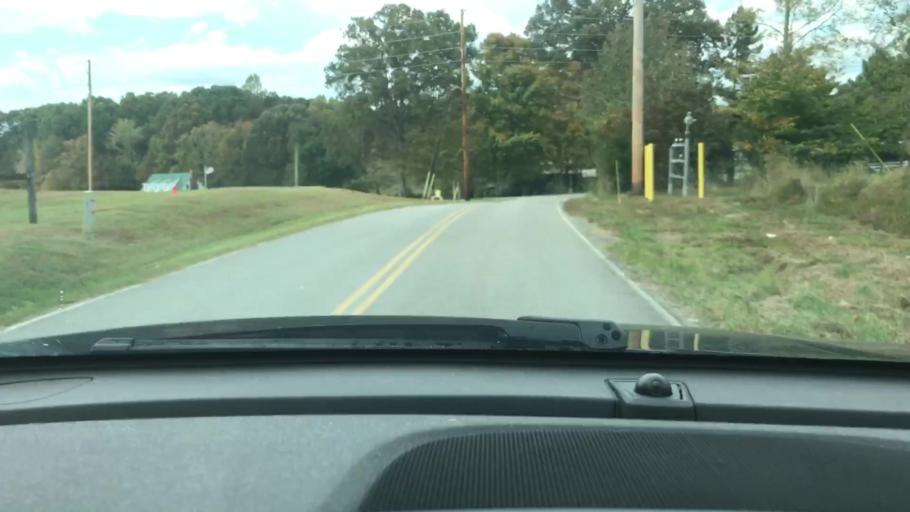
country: US
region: Tennessee
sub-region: Dickson County
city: Charlotte
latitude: 36.1968
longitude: -87.2939
